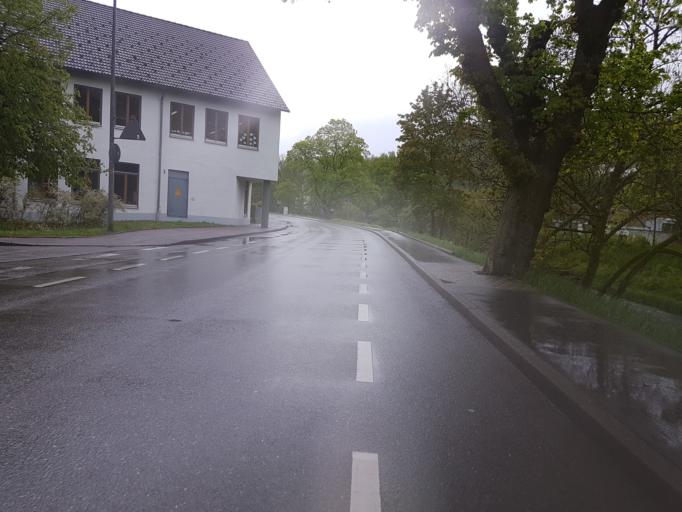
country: DE
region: Baden-Wuerttemberg
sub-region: Freiburg Region
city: Oberndorf
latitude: 48.2910
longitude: 8.5781
